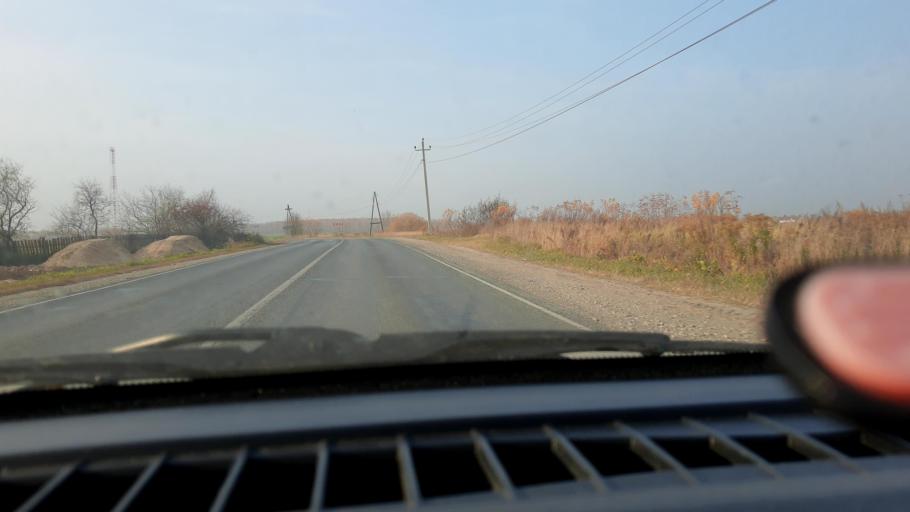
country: RU
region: Nizjnij Novgorod
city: Gorodets
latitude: 56.6369
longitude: 43.5258
